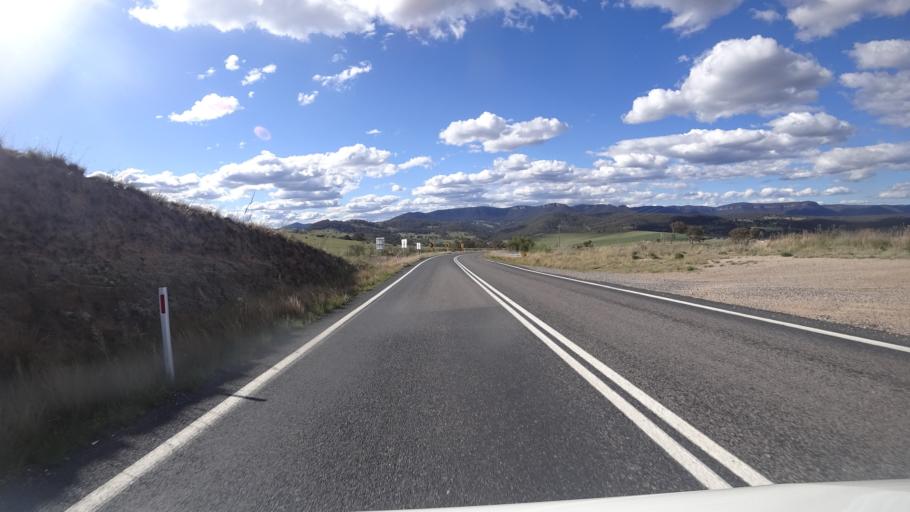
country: AU
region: New South Wales
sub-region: Lithgow
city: Bowenfels
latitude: -33.5653
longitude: 150.1315
